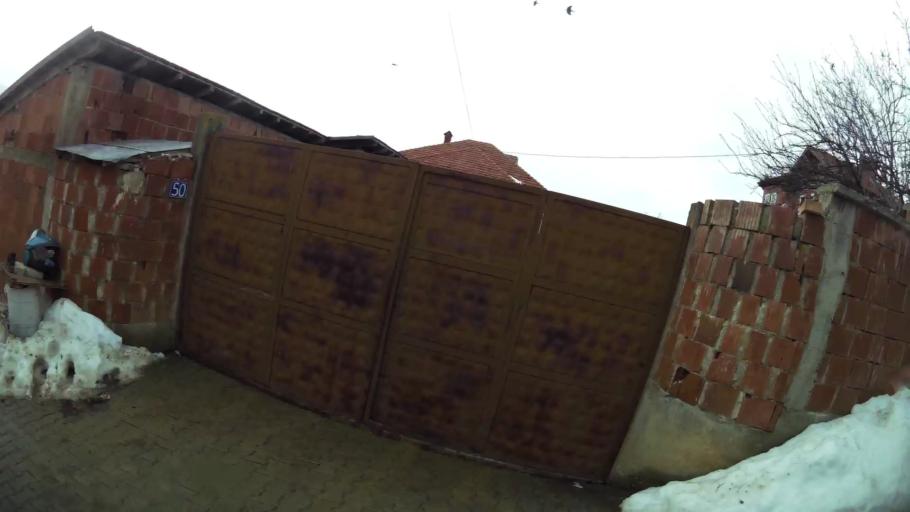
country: XK
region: Pristina
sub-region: Komuna e Prishtines
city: Pristina
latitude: 42.6885
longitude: 21.1748
